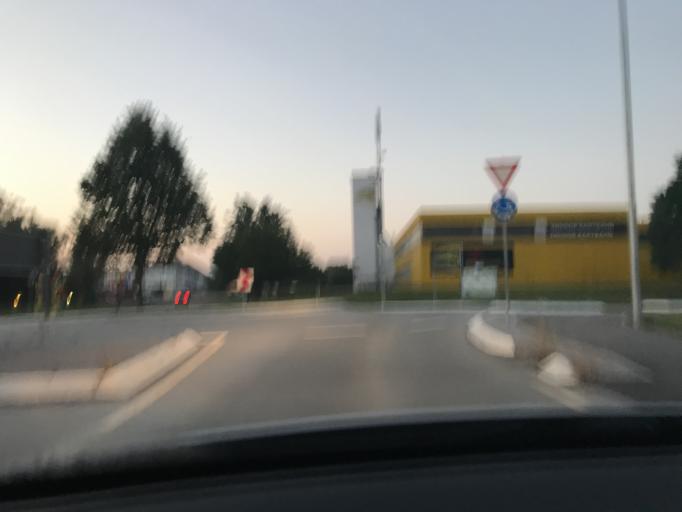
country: DE
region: Baden-Wuerttemberg
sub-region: Regierungsbezirk Stuttgart
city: Gartringen
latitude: 48.6388
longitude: 8.9085
